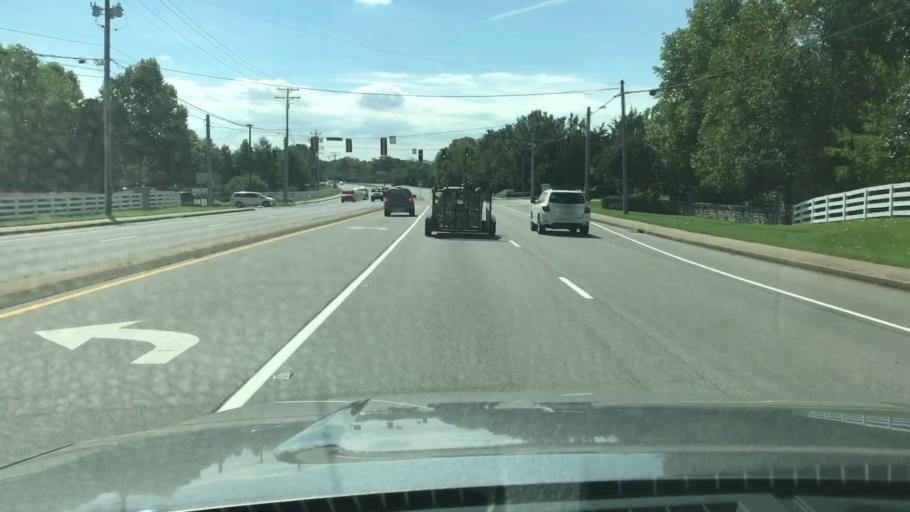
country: US
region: Tennessee
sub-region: Williamson County
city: Franklin
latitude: 35.9640
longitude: -86.8848
